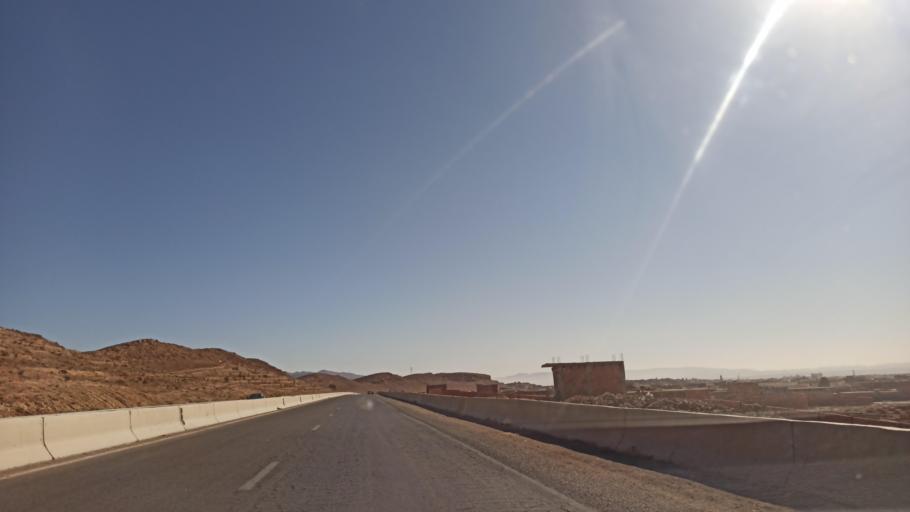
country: TN
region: Gafsa
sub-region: Gafsa Municipality
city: Gafsa
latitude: 34.4501
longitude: 8.7817
